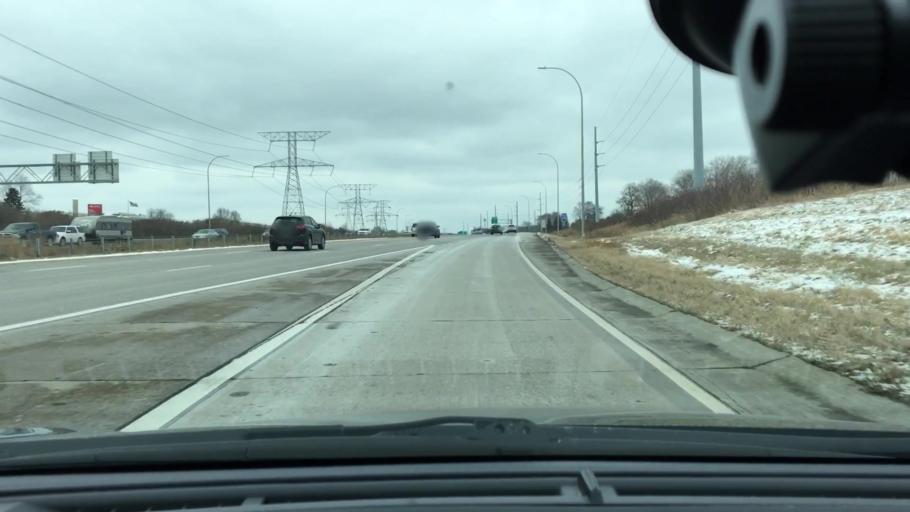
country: US
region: Minnesota
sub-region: Hennepin County
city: Plymouth
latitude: 44.9997
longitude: -93.4575
